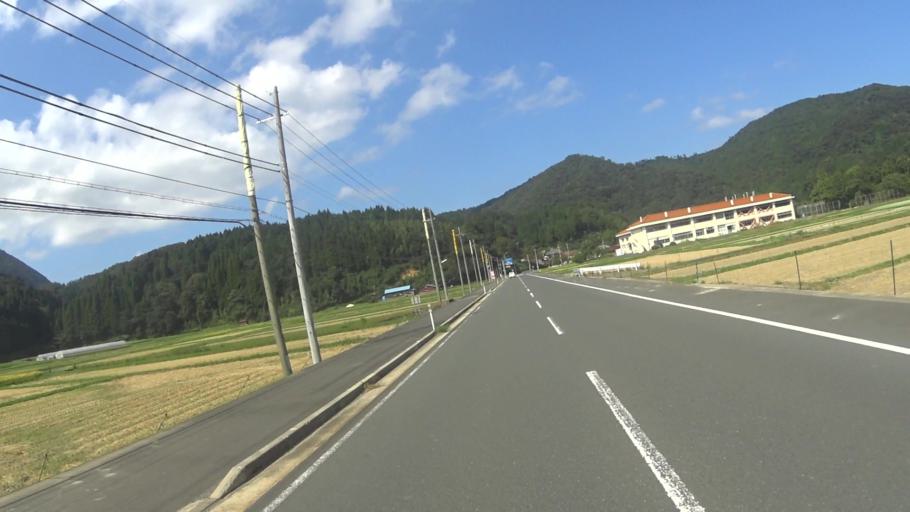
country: JP
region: Kyoto
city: Miyazu
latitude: 35.7267
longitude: 135.2551
